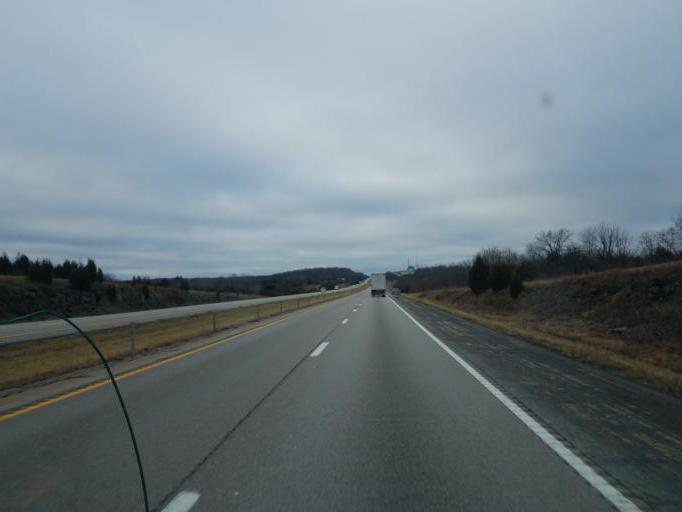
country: US
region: Missouri
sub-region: Laclede County
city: Lebanon
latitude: 37.5756
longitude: -92.7598
